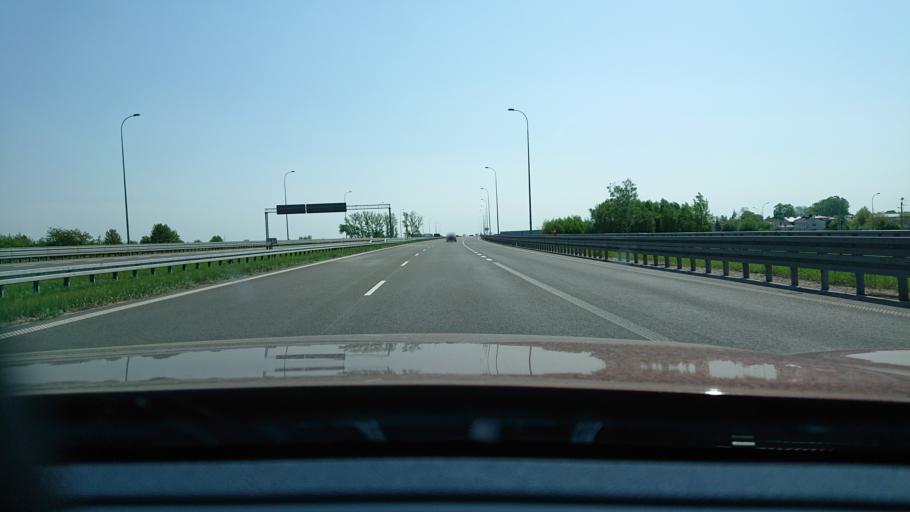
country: PL
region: Subcarpathian Voivodeship
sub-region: Powiat lancucki
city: Lancut
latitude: 50.0992
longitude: 22.2259
